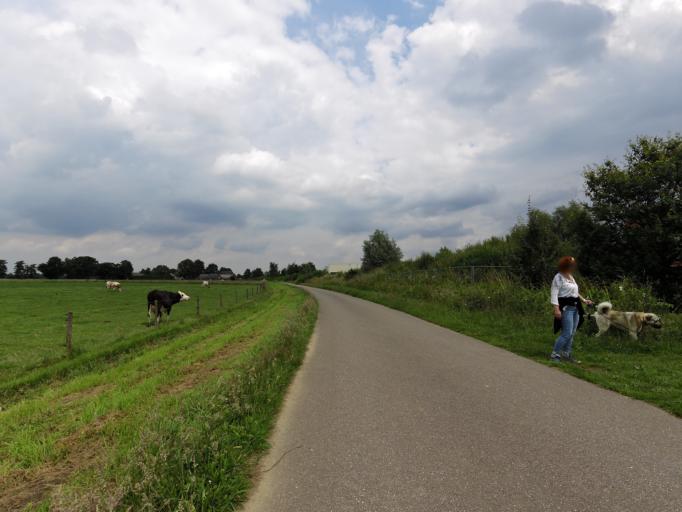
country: NL
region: Gelderland
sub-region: Gemeente Zevenaar
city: Zevenaar
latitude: 51.9306
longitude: 6.1123
